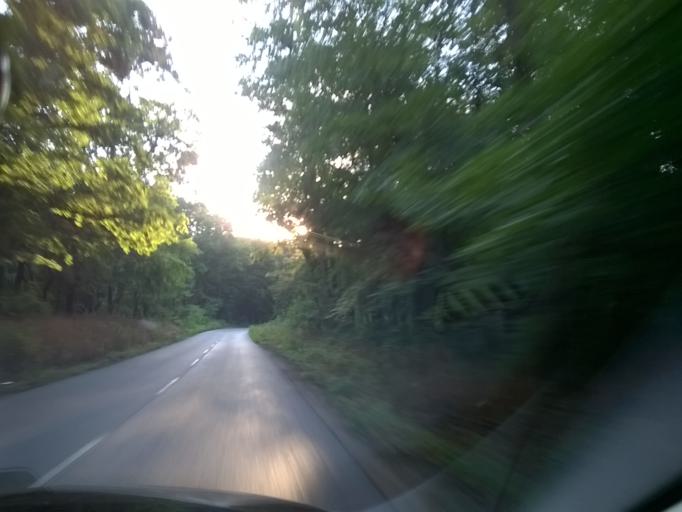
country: SK
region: Nitriansky
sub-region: Okres Nitra
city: Nitra
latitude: 48.2833
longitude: 17.9832
